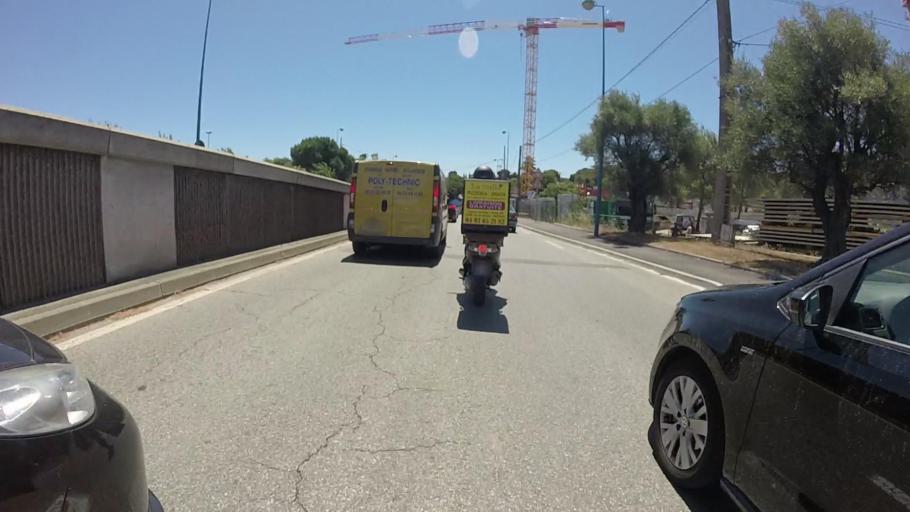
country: FR
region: Provence-Alpes-Cote d'Azur
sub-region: Departement des Alpes-Maritimes
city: Biot
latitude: 43.6004
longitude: 7.0853
